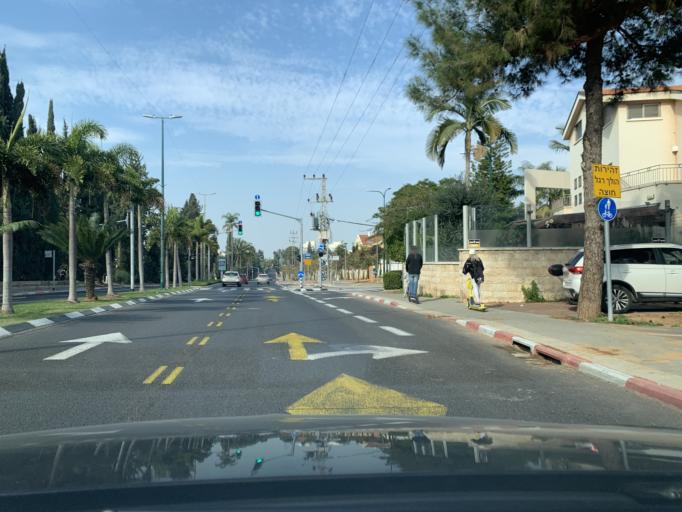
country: IL
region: Tel Aviv
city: Giv`at Shemu'el
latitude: 32.0567
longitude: 34.8509
